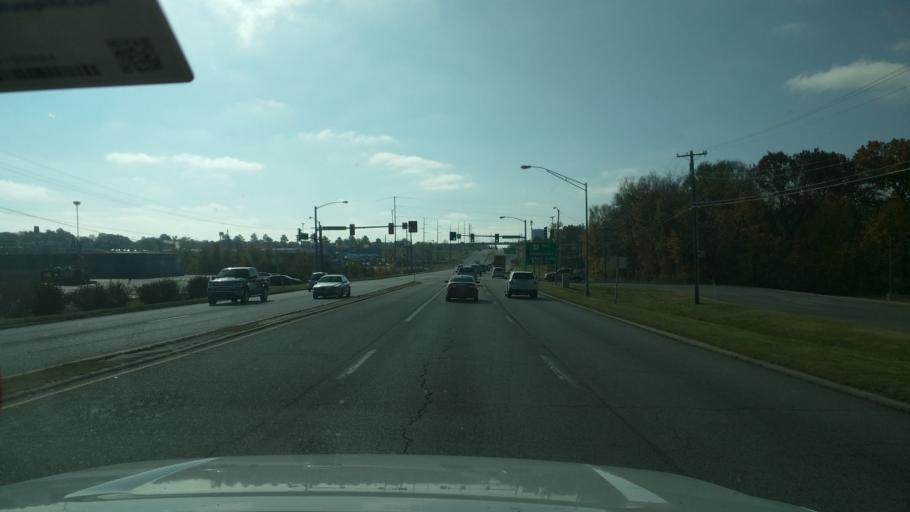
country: US
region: Oklahoma
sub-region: Washington County
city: Bartlesville
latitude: 36.7493
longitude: -95.9355
